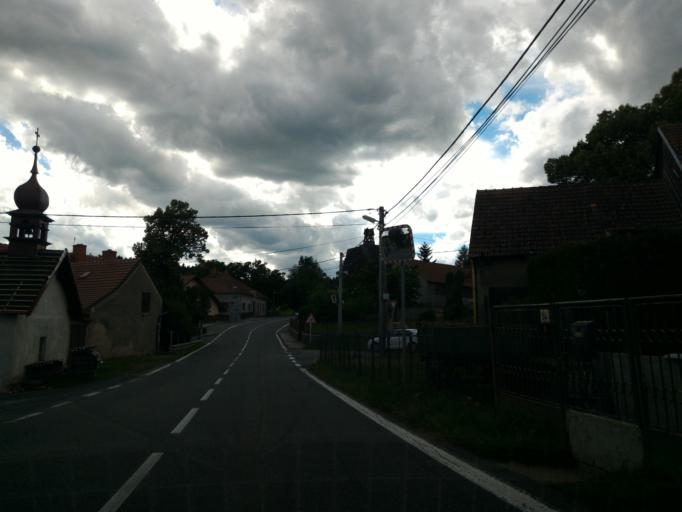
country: CZ
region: Vysocina
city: Bohdalov
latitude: 49.4773
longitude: 15.8309
